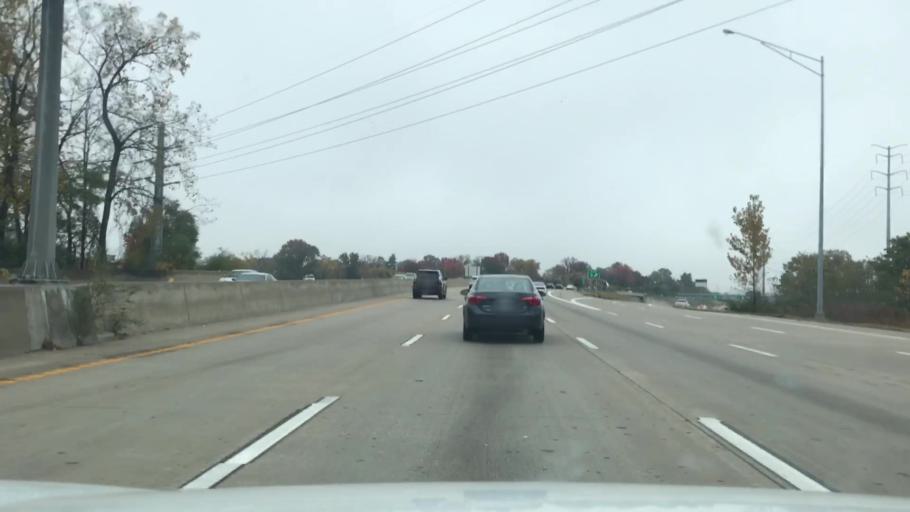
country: US
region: Missouri
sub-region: Saint Louis County
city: Olivette
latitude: 38.6713
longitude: -90.3619
